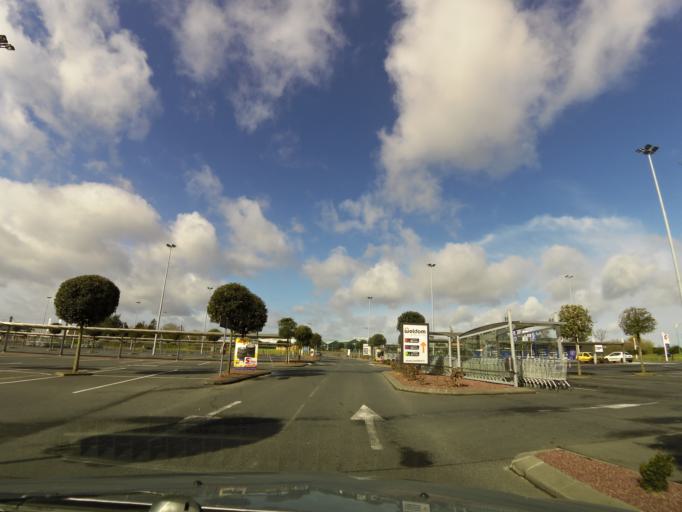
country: FR
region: Lower Normandy
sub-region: Departement de la Manche
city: Agneaux
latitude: 49.1079
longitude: -1.1353
